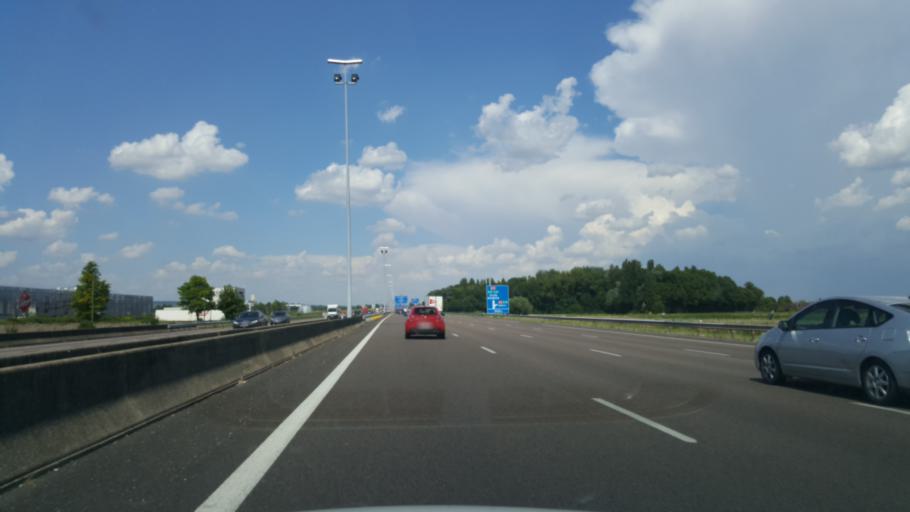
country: FR
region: Bourgogne
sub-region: Departement de la Cote-d'Or
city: Bligny-les-Beaune
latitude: 47.0035
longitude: 4.8613
